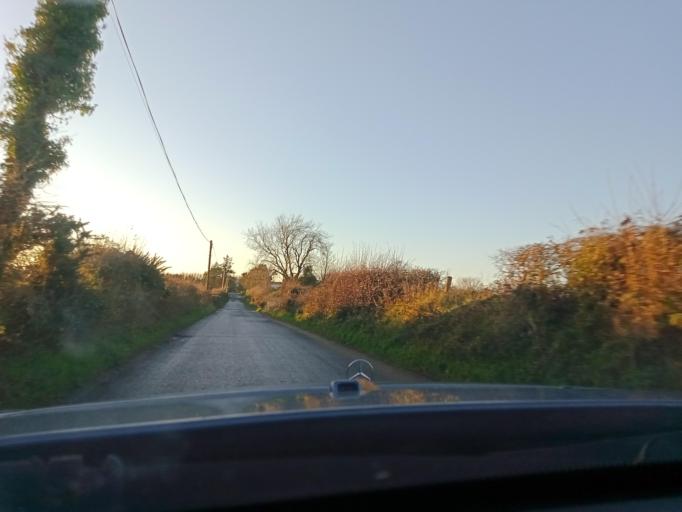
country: IE
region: Munster
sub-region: Waterford
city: Waterford
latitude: 52.3735
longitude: -7.1364
